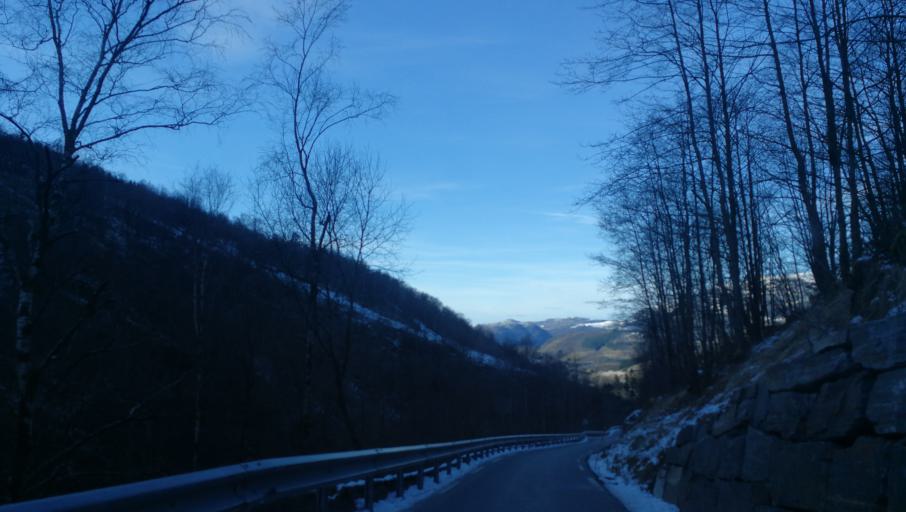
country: NO
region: Rogaland
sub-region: Hjelmeland
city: Hjelmelandsvagen
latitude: 59.1239
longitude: 6.2737
